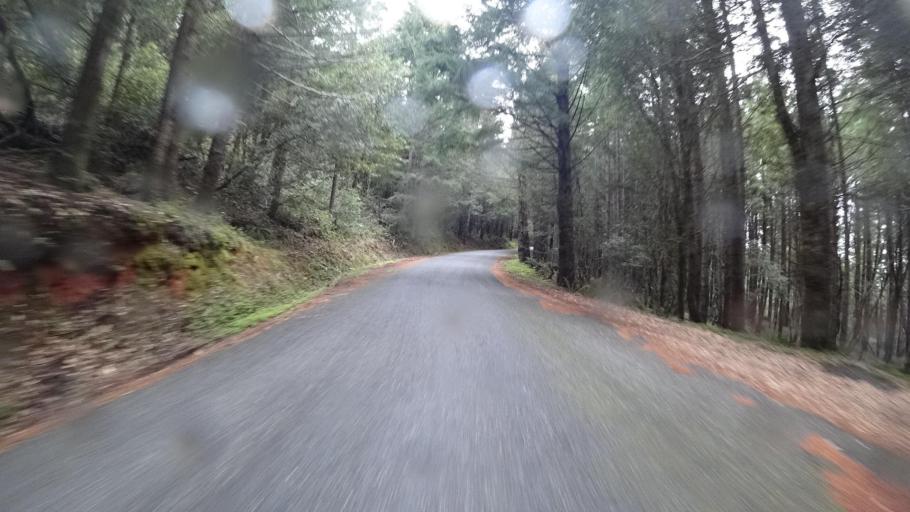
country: US
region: California
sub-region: Humboldt County
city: Willow Creek
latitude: 41.2006
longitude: -123.7791
